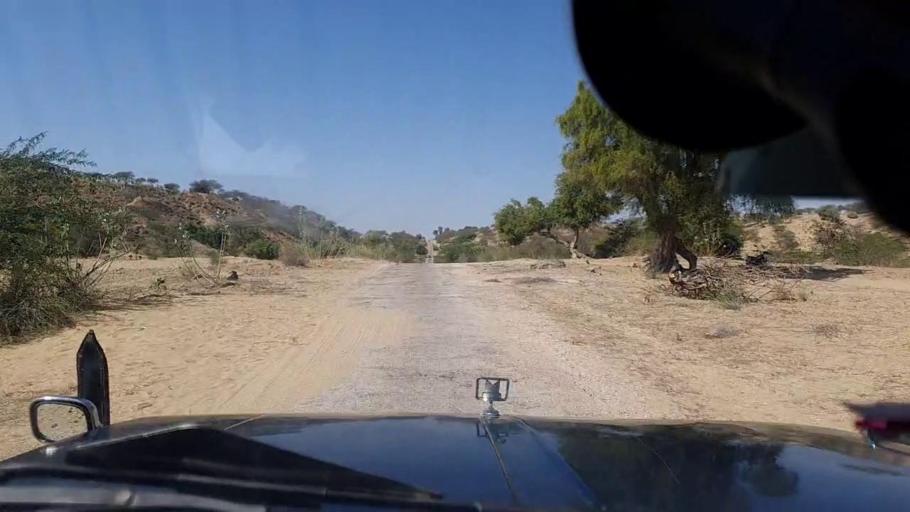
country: PK
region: Sindh
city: Mithi
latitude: 24.6122
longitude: 69.7154
